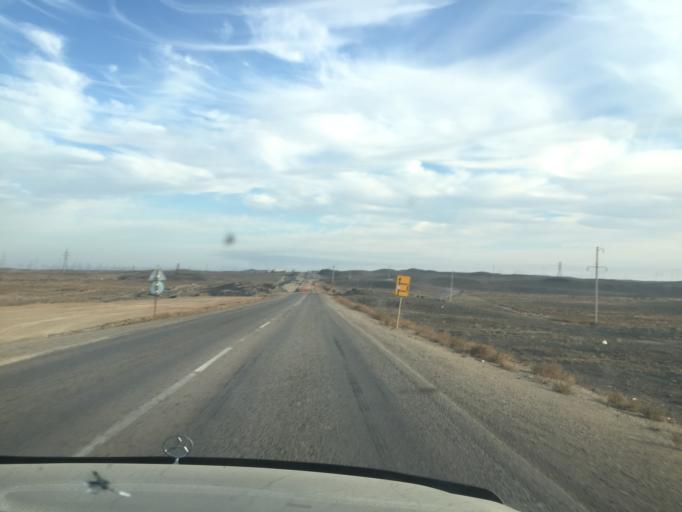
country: KZ
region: Almaty Oblysy
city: Ulken
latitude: 45.2108
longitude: 73.8764
